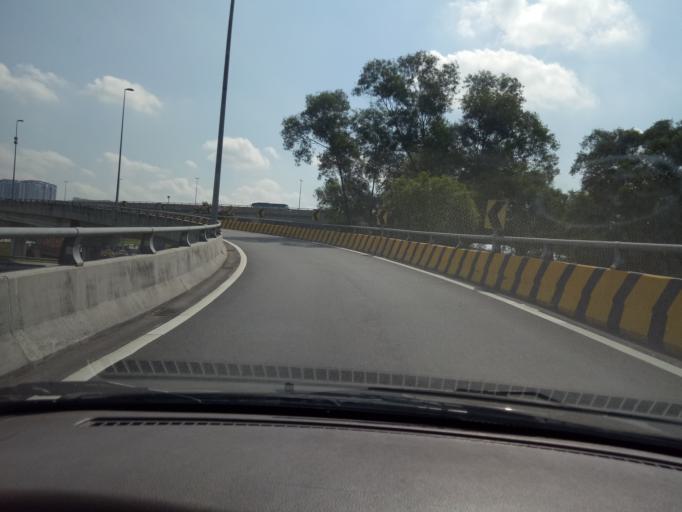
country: MY
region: Selangor
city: Kampong Baharu Balakong
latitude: 3.0616
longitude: 101.6832
